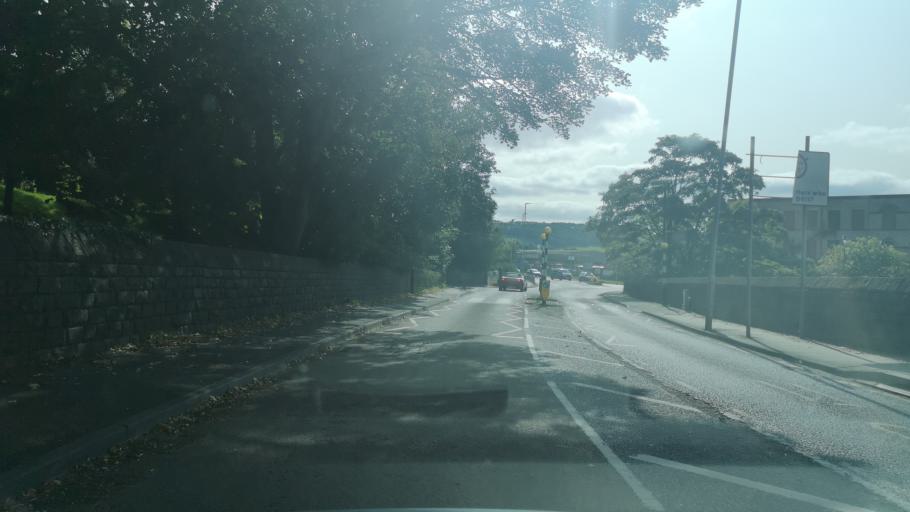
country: GB
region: England
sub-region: Kirklees
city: Dewsbury
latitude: 53.6792
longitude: -1.6360
